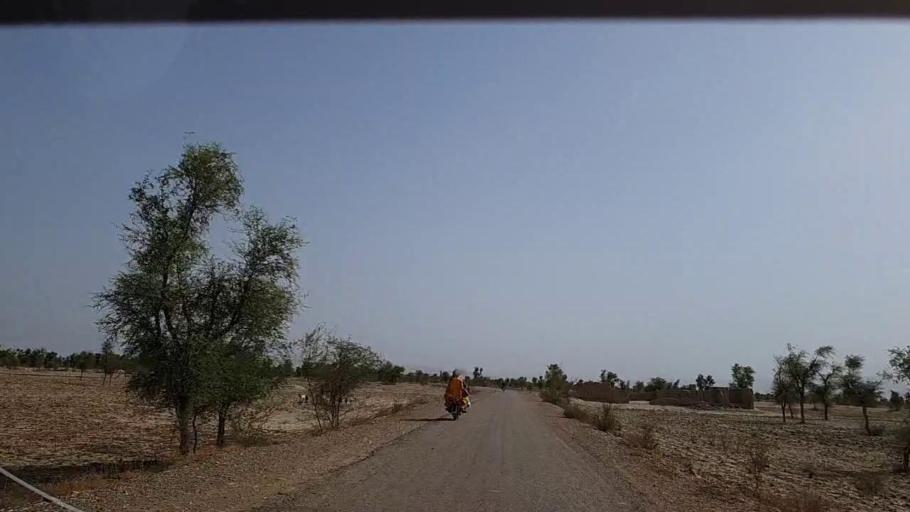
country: PK
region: Sindh
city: Johi
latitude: 26.6184
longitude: 67.4970
